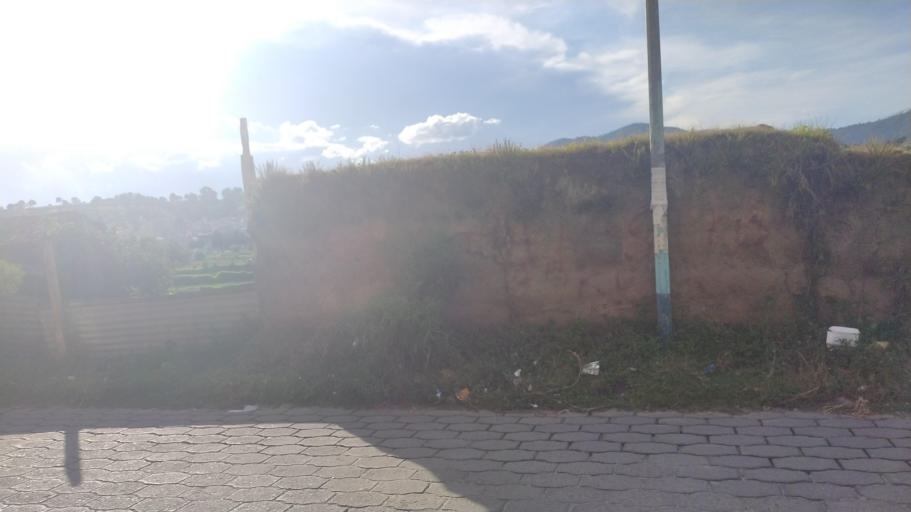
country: GT
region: Quetzaltenango
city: Salcaja
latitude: 14.8741
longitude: -91.4575
